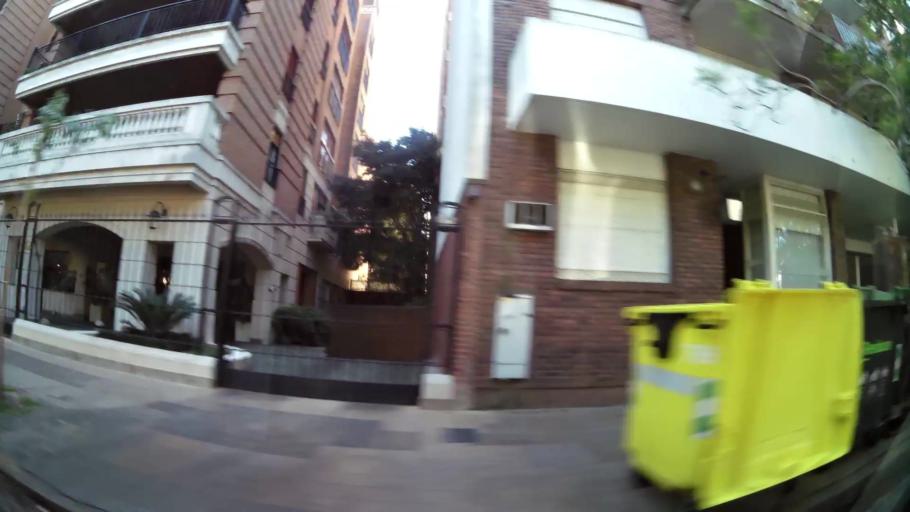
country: AR
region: Buenos Aires
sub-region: Partido de San Isidro
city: San Isidro
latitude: -34.4727
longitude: -58.5098
